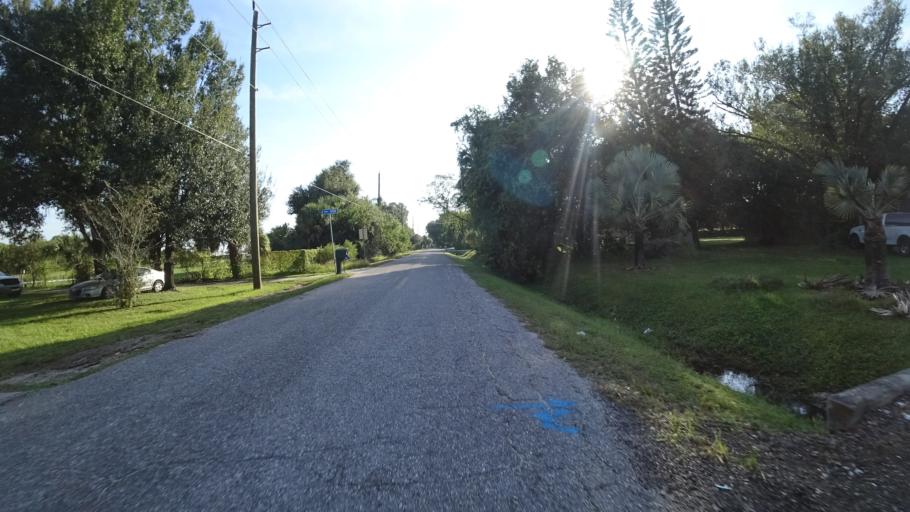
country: US
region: Florida
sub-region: Manatee County
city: Samoset
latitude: 27.4692
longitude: -82.5000
